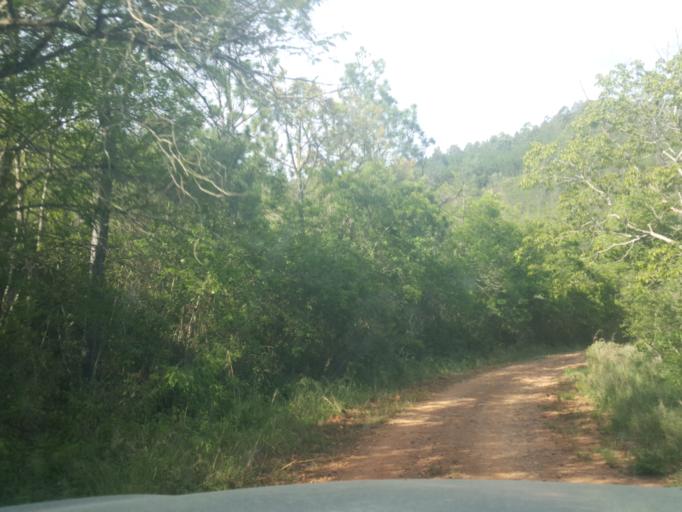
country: ZA
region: Limpopo
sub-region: Mopani District Municipality
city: Hoedspruit
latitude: -24.5918
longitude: 30.8358
